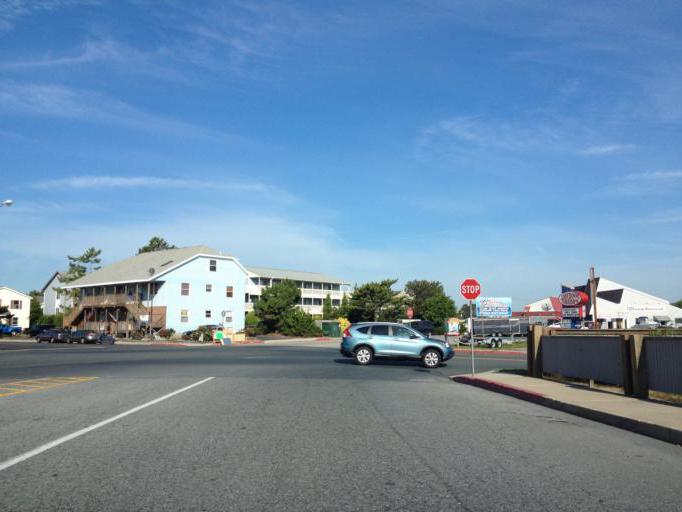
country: US
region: Delaware
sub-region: Sussex County
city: Bethany Beach
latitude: 38.4511
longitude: -75.0619
